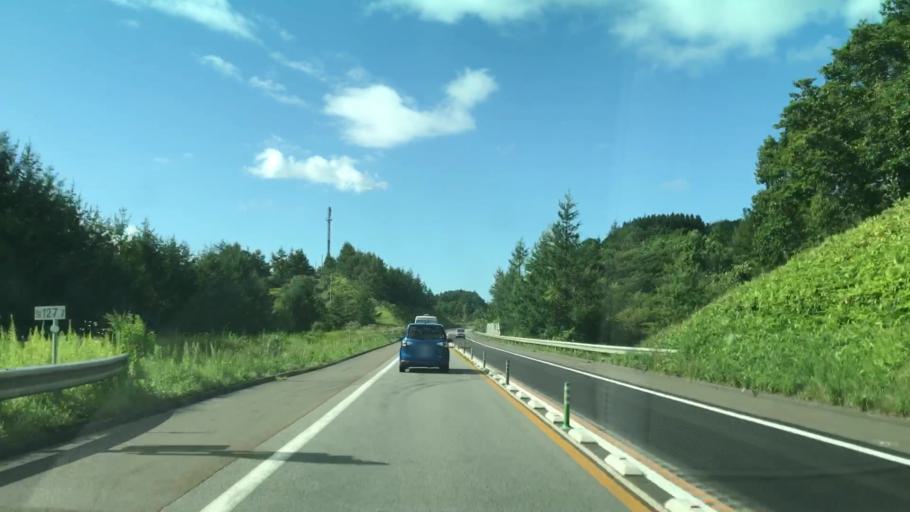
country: JP
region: Hokkaido
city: Date
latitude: 42.4402
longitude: 140.9181
